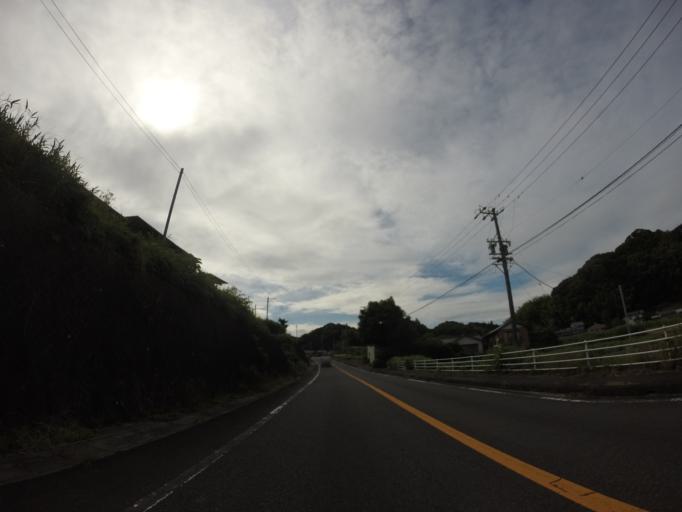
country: JP
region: Shizuoka
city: Shimada
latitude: 34.7853
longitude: 138.1550
